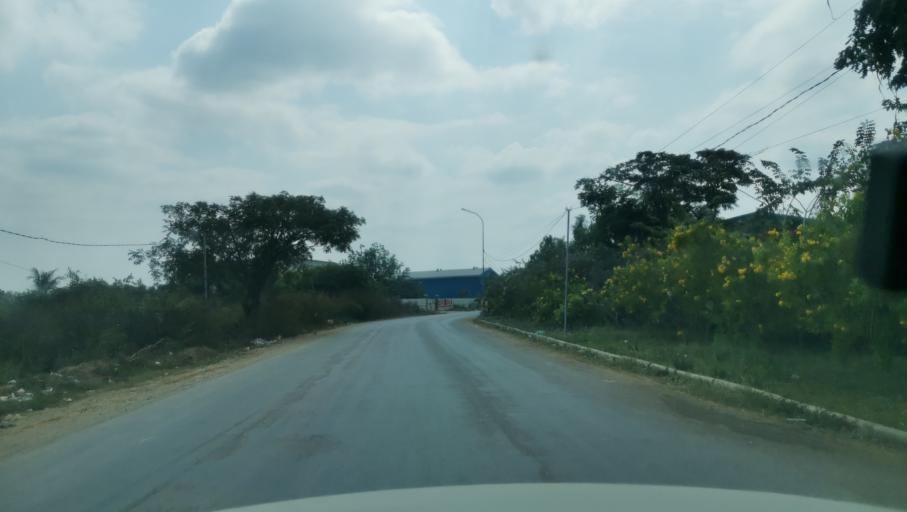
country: KH
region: Battambang
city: Battambang
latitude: 13.0783
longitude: 103.1864
